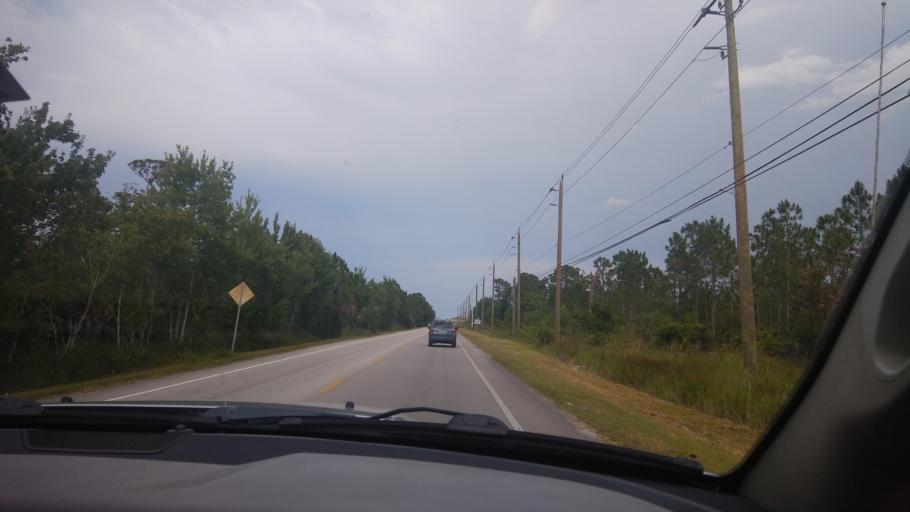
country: US
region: Florida
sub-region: Indian River County
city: Fellsmere
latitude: 27.7676
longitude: -80.5611
